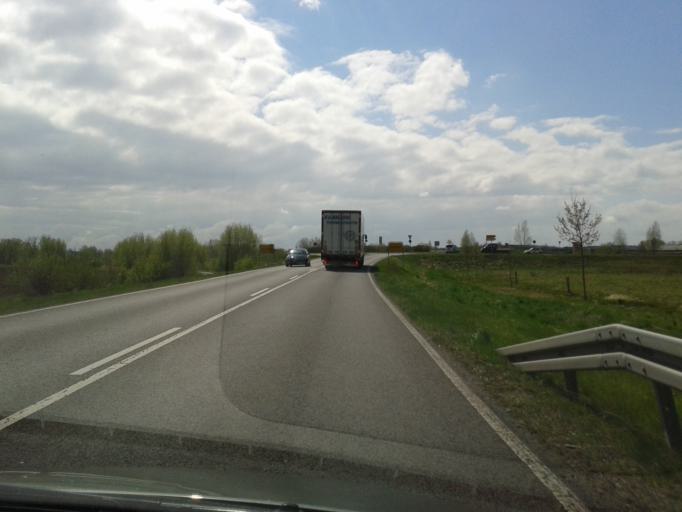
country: DE
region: Saxony-Anhalt
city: Salzwedel
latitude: 52.8607
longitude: 11.1757
